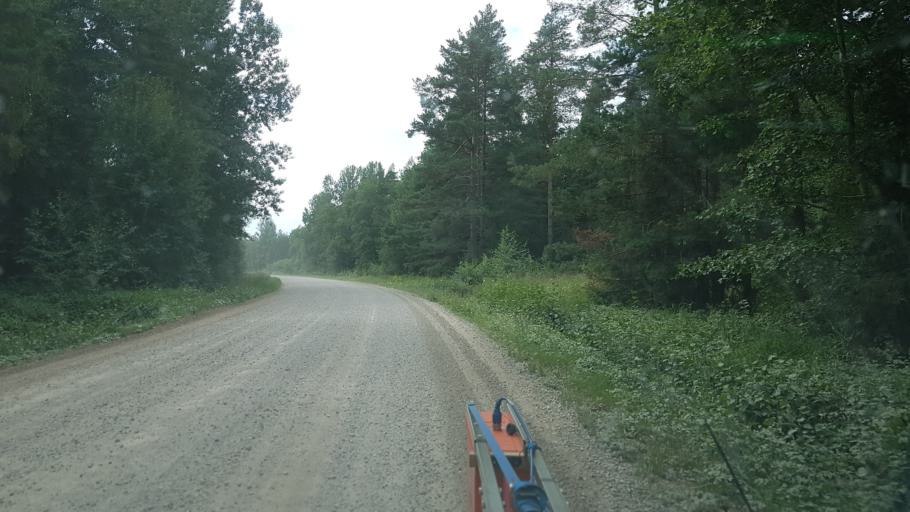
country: EE
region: Paernumaa
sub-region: Halinga vald
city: Parnu-Jaagupi
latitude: 58.5412
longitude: 24.4087
